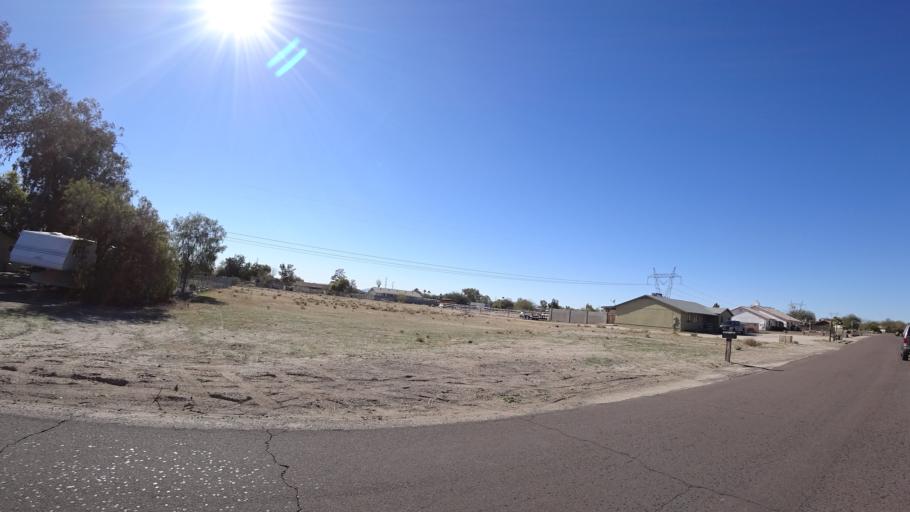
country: US
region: Arizona
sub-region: Maricopa County
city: Buckeye
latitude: 33.4248
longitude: -112.5318
